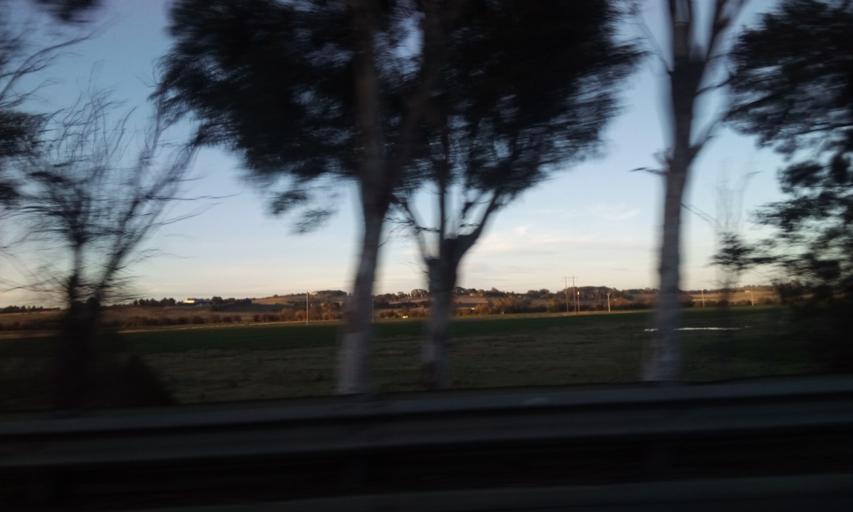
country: AU
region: New South Wales
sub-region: Goulburn Mulwaree
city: Goulburn
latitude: -34.7762
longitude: 149.7142
